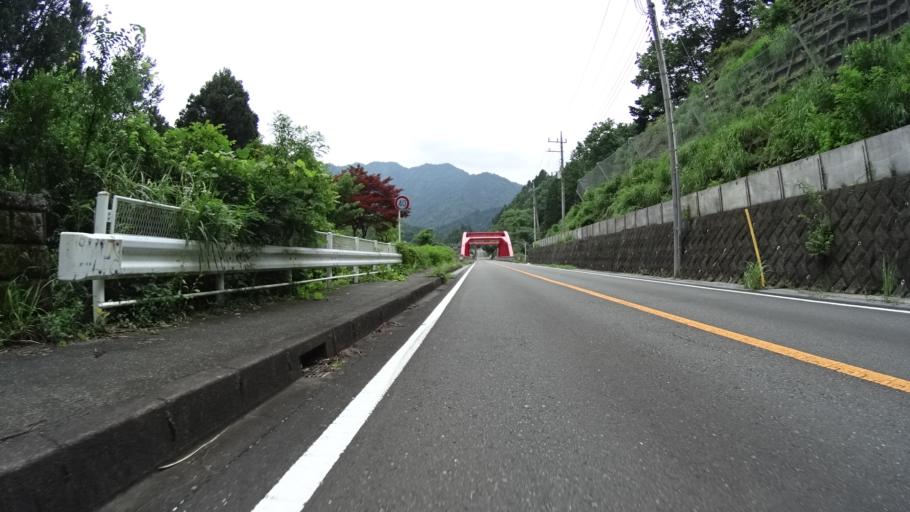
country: JP
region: Kanagawa
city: Hadano
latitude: 35.5114
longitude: 139.2313
